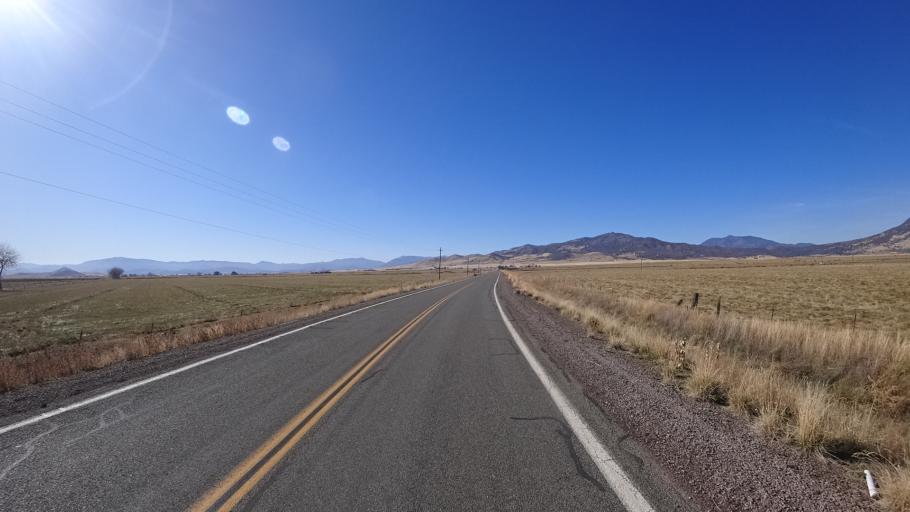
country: US
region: California
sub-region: Siskiyou County
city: Montague
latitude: 41.7938
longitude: -122.4563
